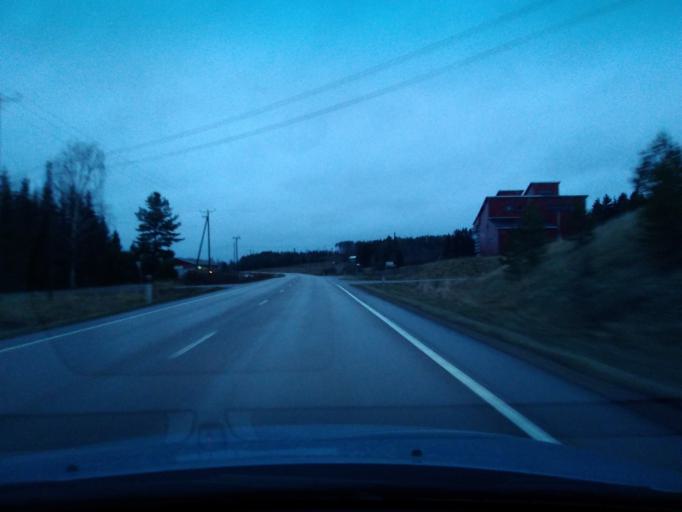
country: FI
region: Uusimaa
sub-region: Porvoo
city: Askola
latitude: 60.4603
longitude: 25.5793
